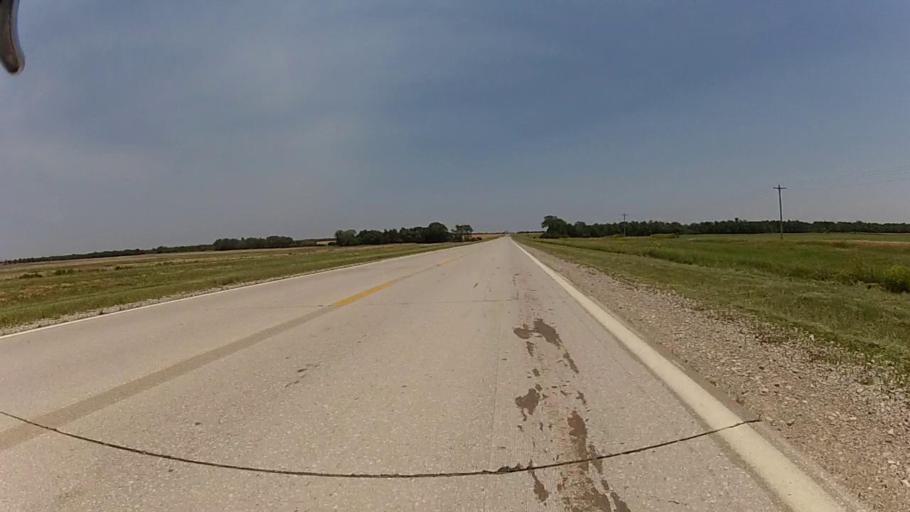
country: US
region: Kansas
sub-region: Sumner County
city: Wellington
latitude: 37.0574
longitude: -97.2915
